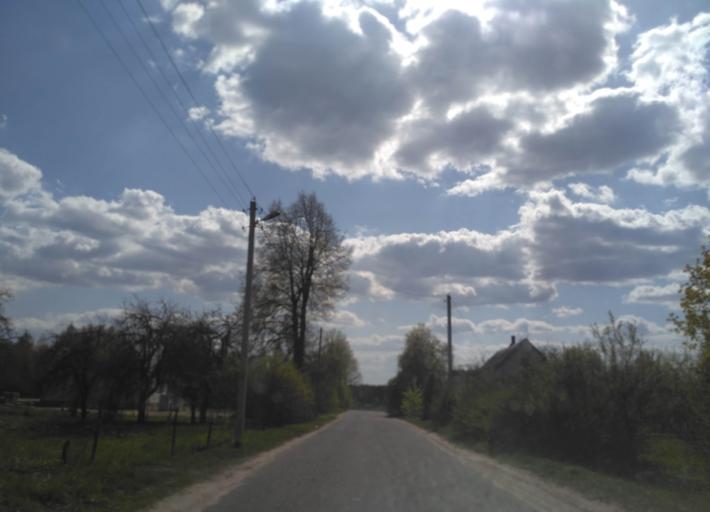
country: BY
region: Minsk
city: Narach
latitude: 54.9713
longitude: 26.6382
